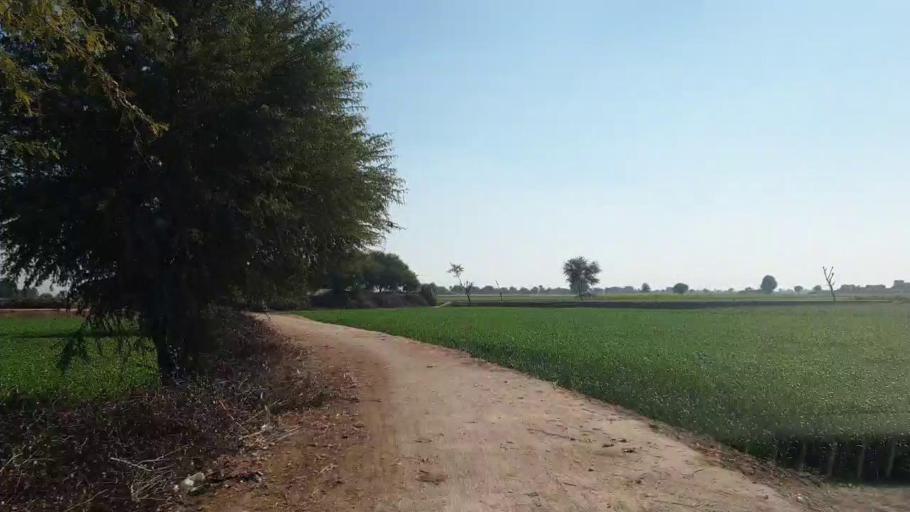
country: PK
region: Sindh
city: Shahpur Chakar
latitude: 26.1232
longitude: 68.6443
